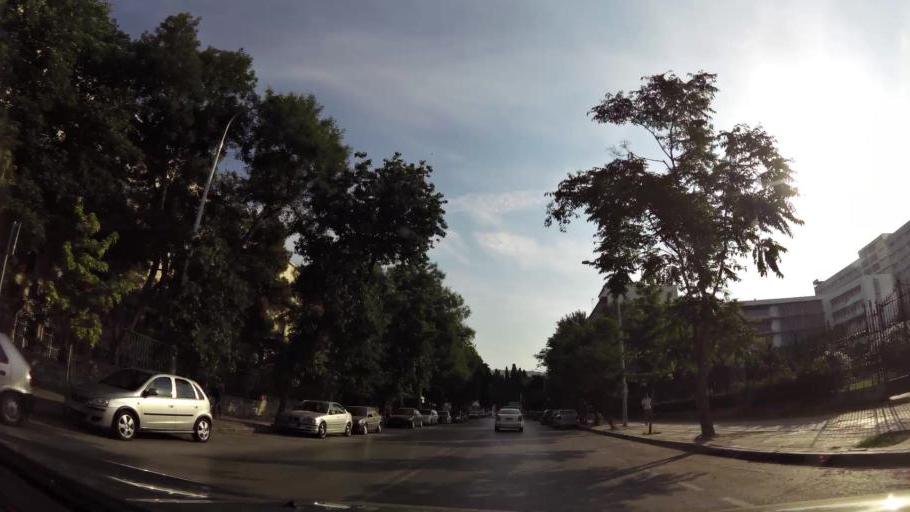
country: GR
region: Central Macedonia
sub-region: Nomos Thessalonikis
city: Agios Pavlos
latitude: 40.6331
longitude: 22.9553
